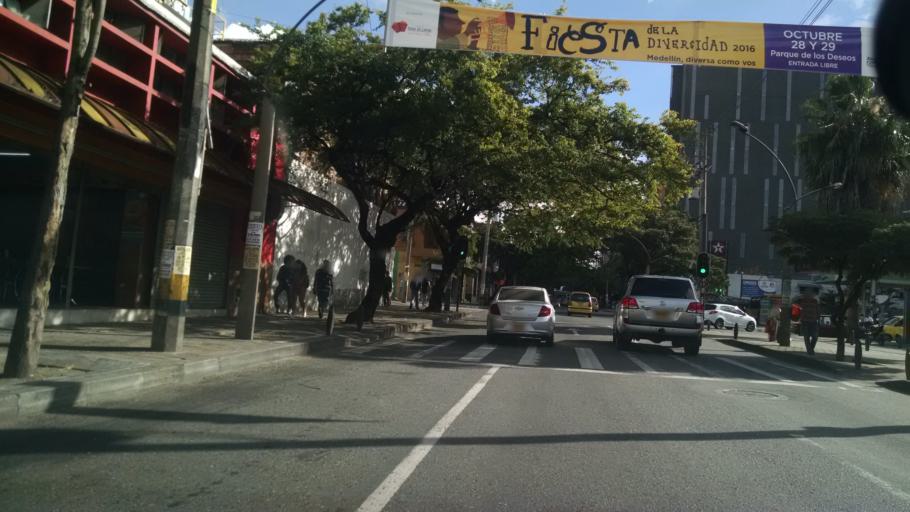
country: CO
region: Antioquia
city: Medellin
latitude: 6.2667
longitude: -75.5660
